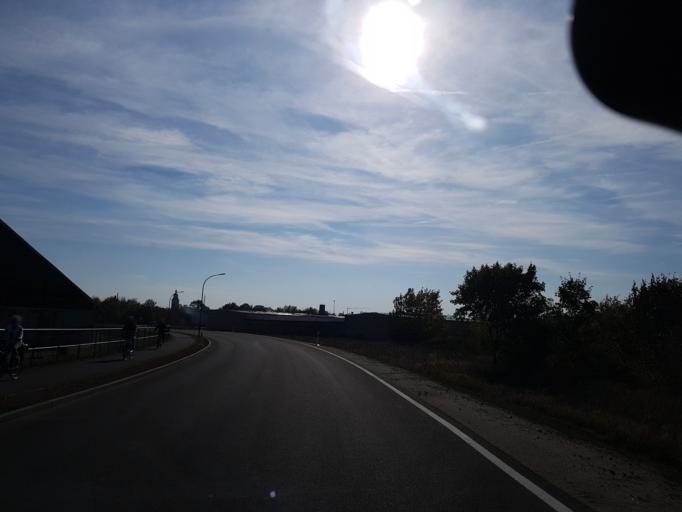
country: DE
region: Brandenburg
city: Finsterwalde
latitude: 51.6426
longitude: 13.7143
